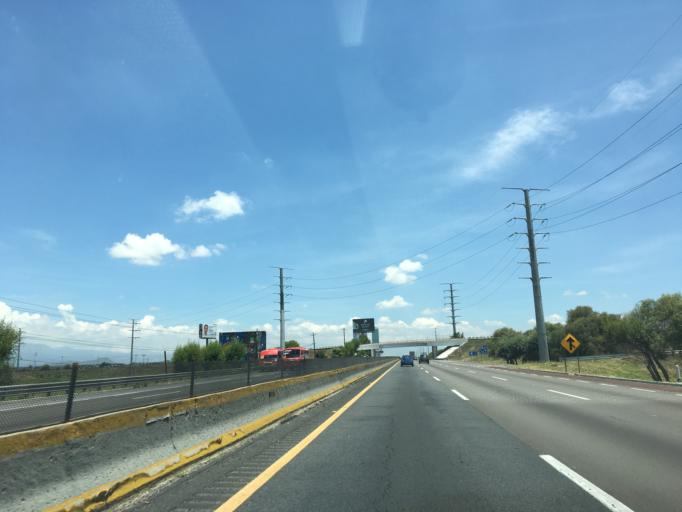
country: MX
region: Puebla
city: Santa Ana Xalmimilulco
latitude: 19.2130
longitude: -98.3540
